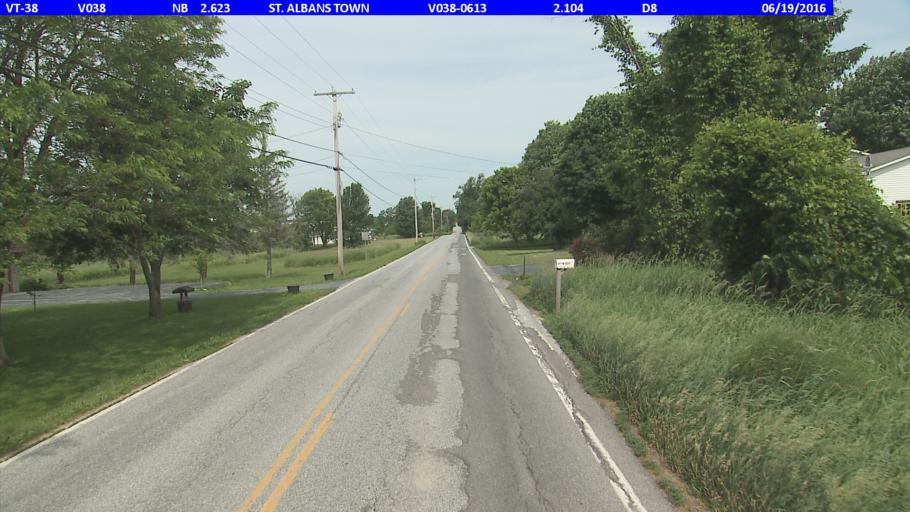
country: US
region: Vermont
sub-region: Franklin County
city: Saint Albans
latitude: 44.8475
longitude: -73.1148
